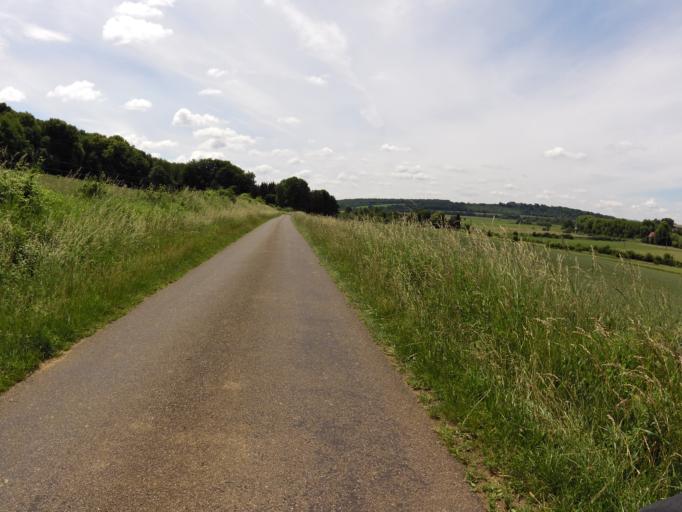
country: FR
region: Lorraine
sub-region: Departement de la Meuse
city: Stenay
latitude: 49.5378
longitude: 5.1223
